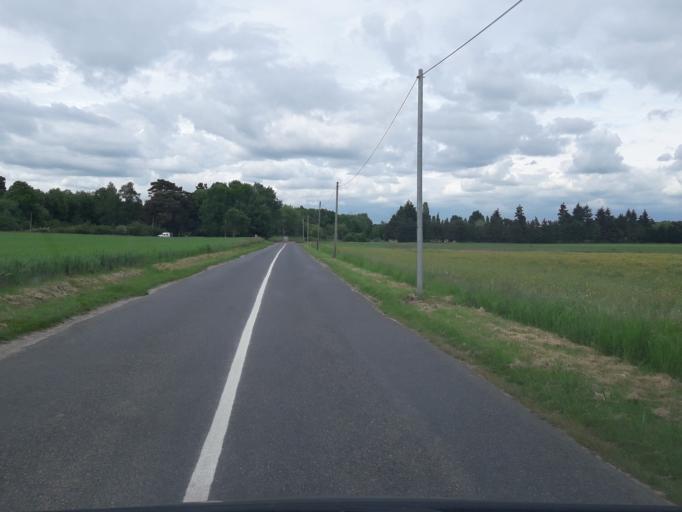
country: FR
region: Ile-de-France
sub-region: Departement de l'Essonne
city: Boissy-le-Cutte
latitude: 48.4345
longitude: 2.2867
